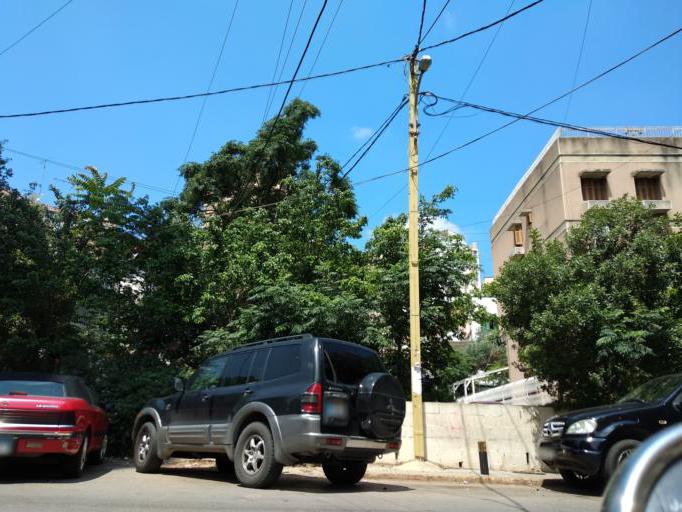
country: LB
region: Mont-Liban
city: Jdaidet el Matn
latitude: 33.8949
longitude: 35.5333
